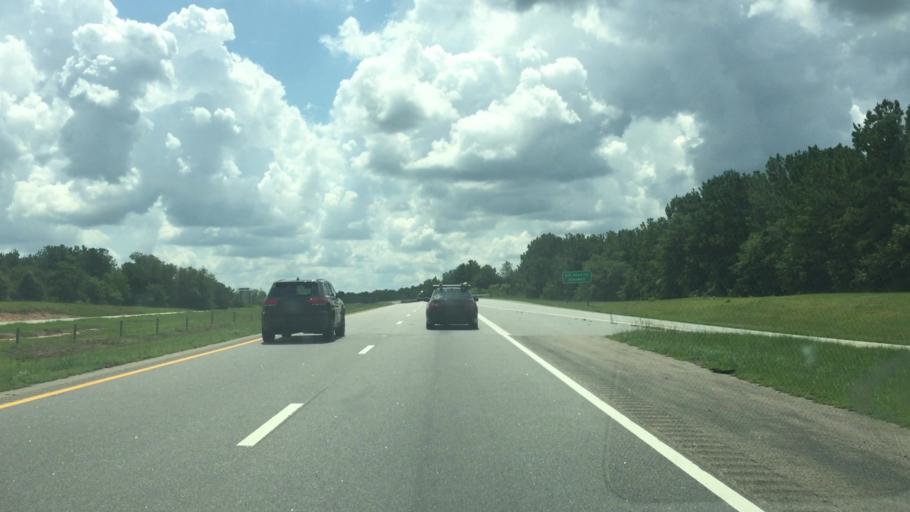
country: US
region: North Carolina
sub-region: Richmond County
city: Hamlet
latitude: 34.8560
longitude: -79.7404
